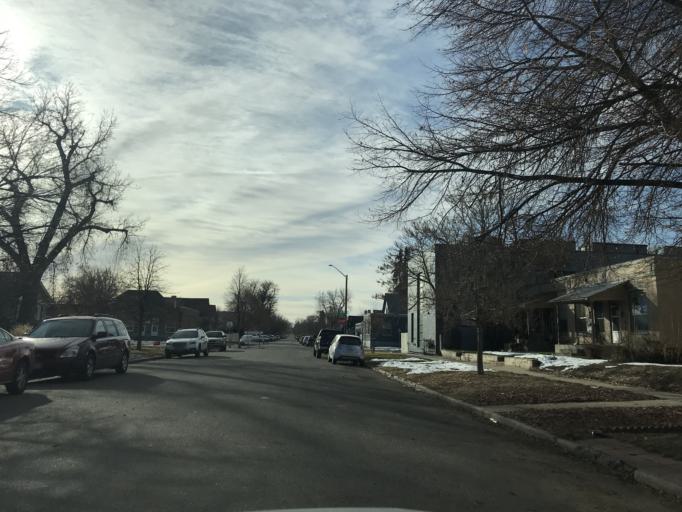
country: US
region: Colorado
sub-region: Denver County
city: Denver
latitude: 39.7707
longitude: -104.9647
